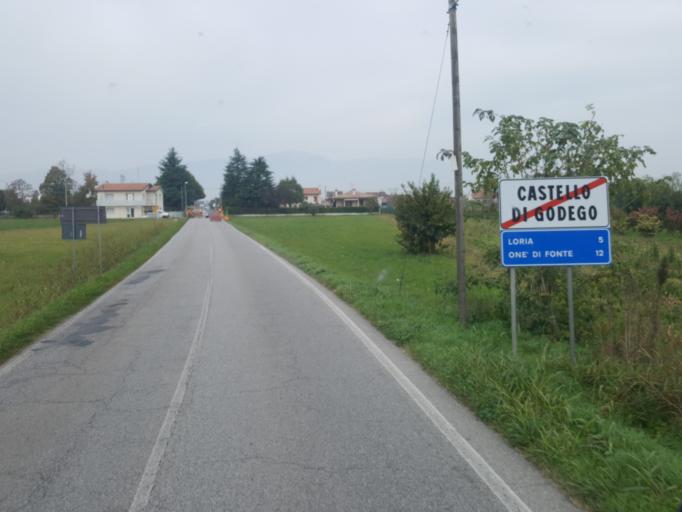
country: IT
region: Veneto
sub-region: Provincia di Treviso
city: Castello di Godego
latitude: 45.6999
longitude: 11.8750
